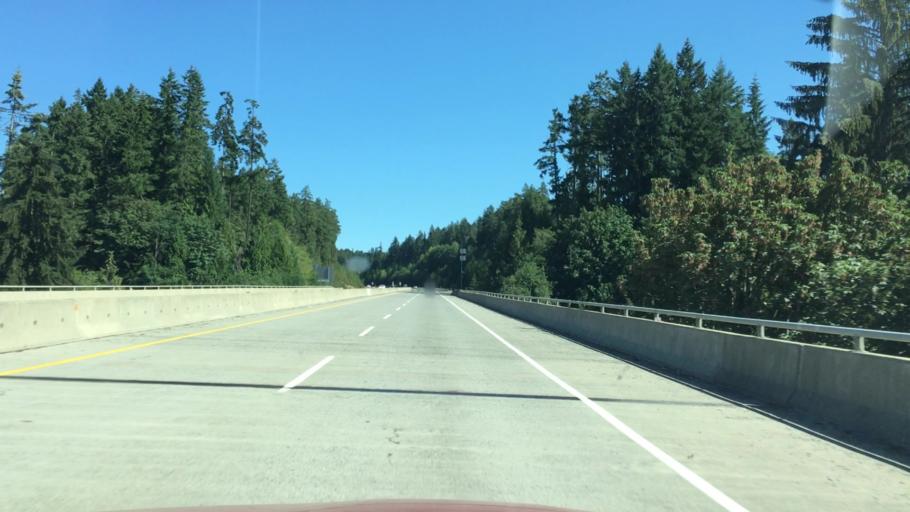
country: CA
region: British Columbia
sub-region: Regional District of Nanaimo
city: Parksville
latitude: 49.3232
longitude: -124.4131
